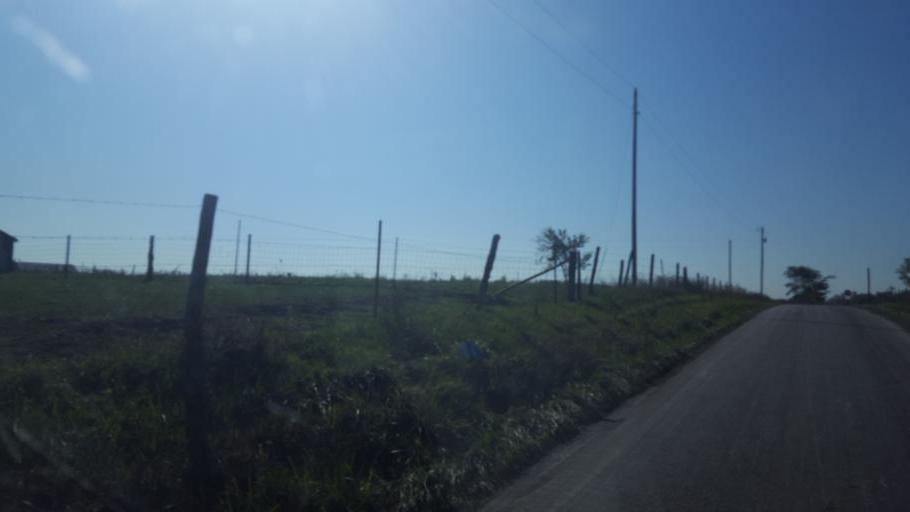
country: US
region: Ohio
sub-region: Hardin County
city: Kenton
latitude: 40.5978
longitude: -83.5544
